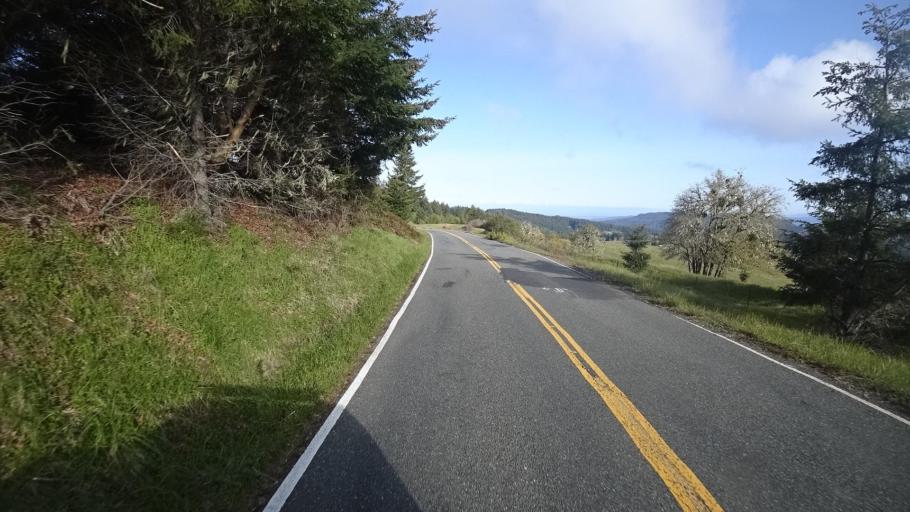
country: US
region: California
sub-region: Humboldt County
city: Blue Lake
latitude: 40.7374
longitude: -123.9469
